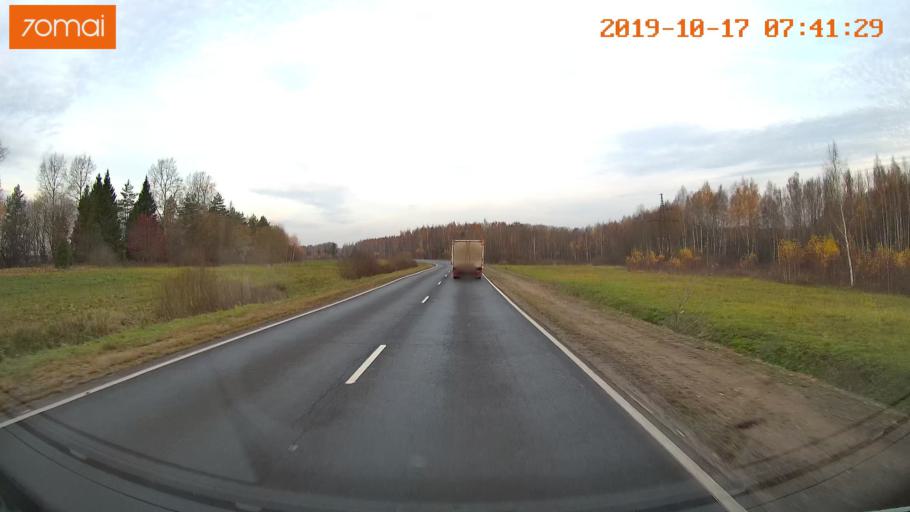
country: RU
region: Vladimir
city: Yur'yev-Pol'skiy
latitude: 56.4823
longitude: 39.8090
